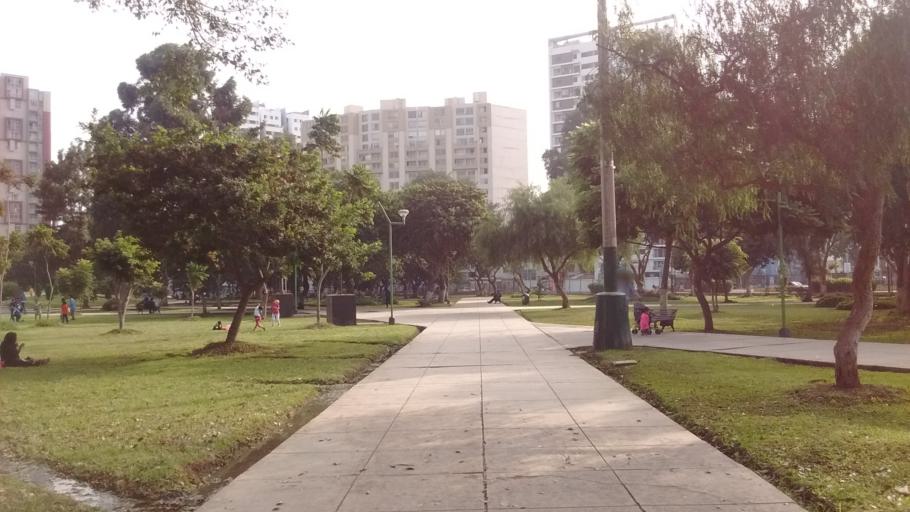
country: PE
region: Lima
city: Lima
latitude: -12.0683
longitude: -77.0429
